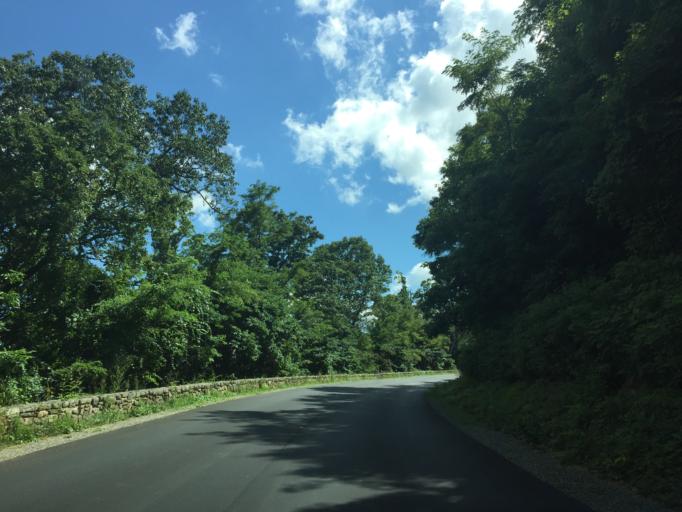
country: US
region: Virginia
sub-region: Page County
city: Luray
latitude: 38.6424
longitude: -78.3115
